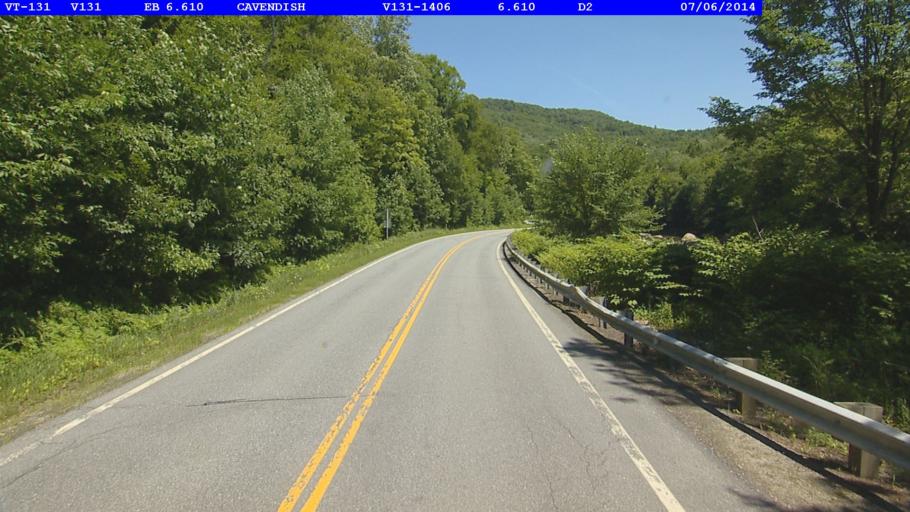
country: US
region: Vermont
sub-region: Windsor County
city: Springfield
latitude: 43.3892
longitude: -72.5550
